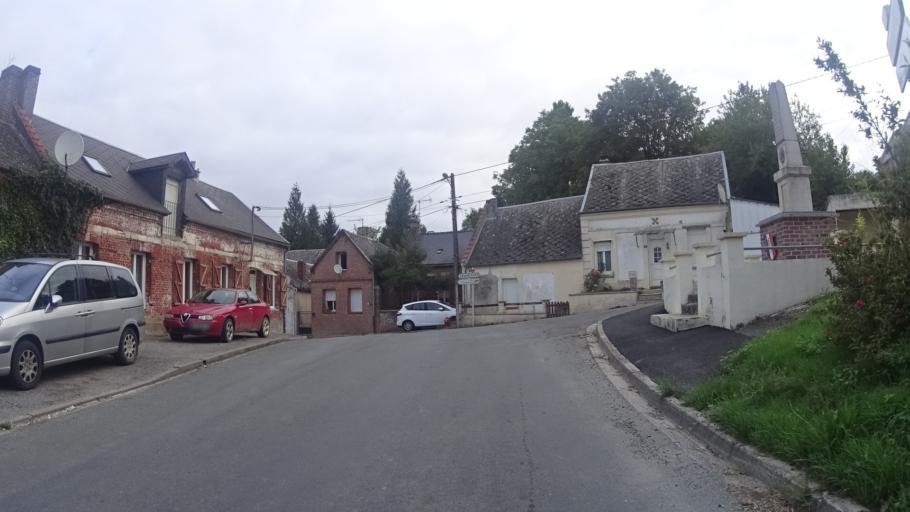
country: FR
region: Picardie
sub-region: Departement de l'Aisne
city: Guise
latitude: 49.9020
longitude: 3.5647
